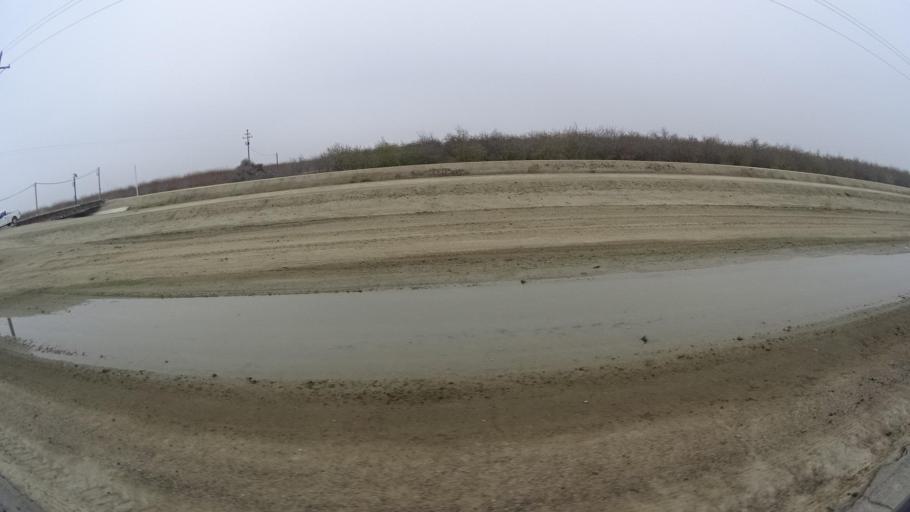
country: US
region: California
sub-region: Kern County
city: Wasco
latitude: 35.6953
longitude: -119.4017
